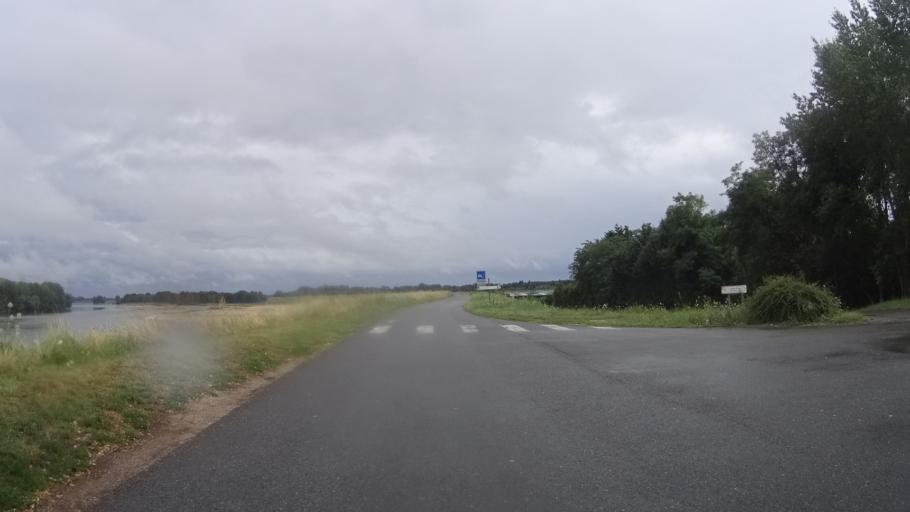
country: FR
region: Centre
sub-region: Departement du Loiret
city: Saint-Jean-de-Braye
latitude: 47.8903
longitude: 1.9944
